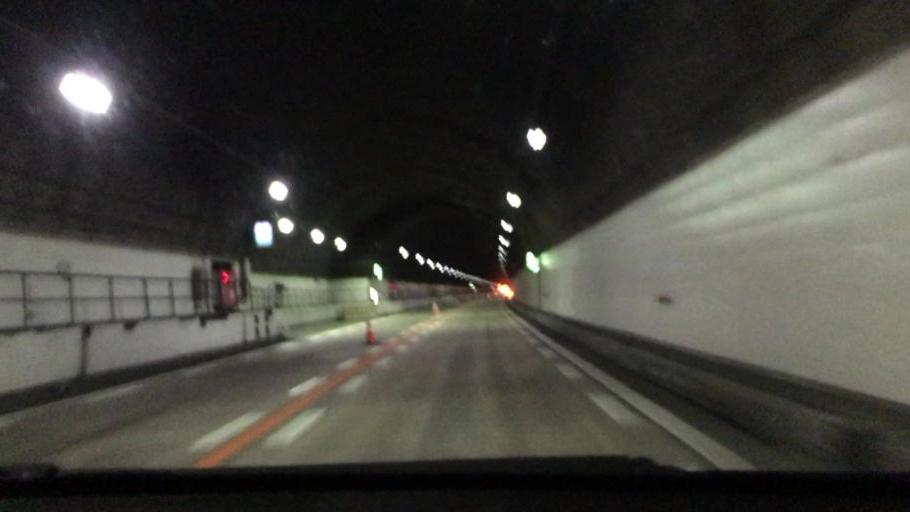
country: JP
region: Yamaguchi
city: Ogori-shimogo
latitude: 34.1050
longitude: 131.4495
